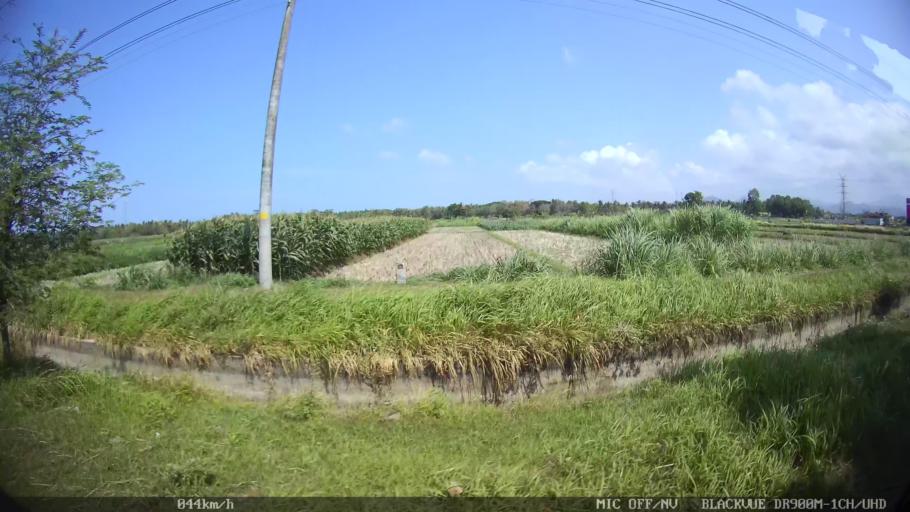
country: ID
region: Daerah Istimewa Yogyakarta
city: Srandakan
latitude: -7.9019
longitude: 110.1523
